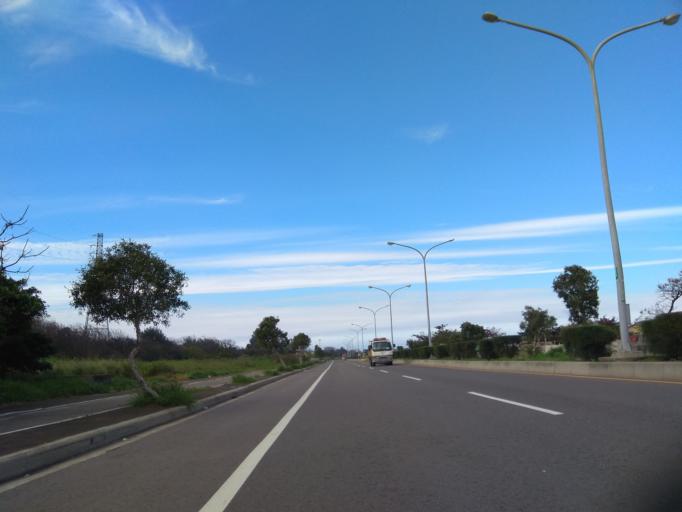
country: TW
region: Taiwan
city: Taoyuan City
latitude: 25.0658
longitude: 121.1754
